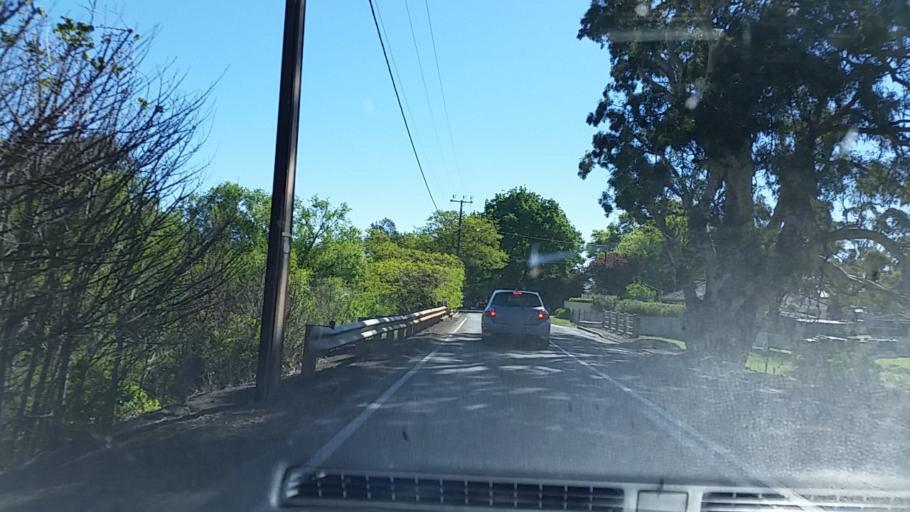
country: AU
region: South Australia
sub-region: Mount Barker
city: Meadows
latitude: -35.1806
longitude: 138.7654
